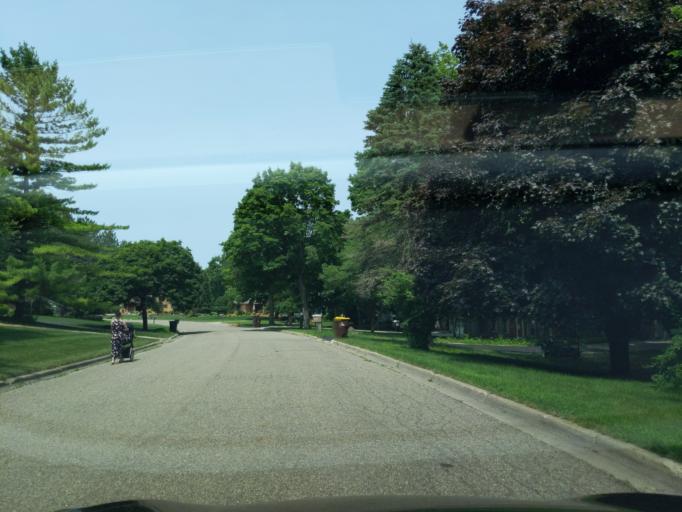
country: US
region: Michigan
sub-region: Eaton County
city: Waverly
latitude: 42.7605
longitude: -84.6431
